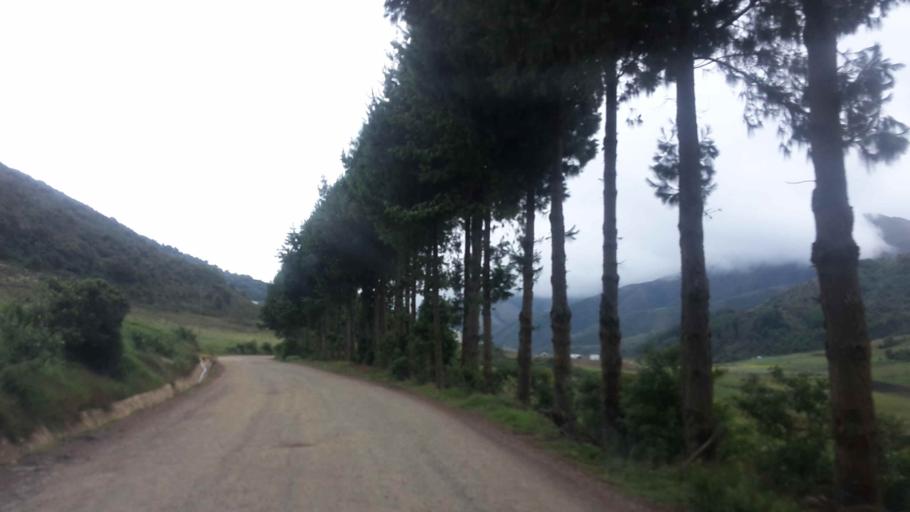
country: BO
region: Cochabamba
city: Totora
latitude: -17.5763
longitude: -65.2876
